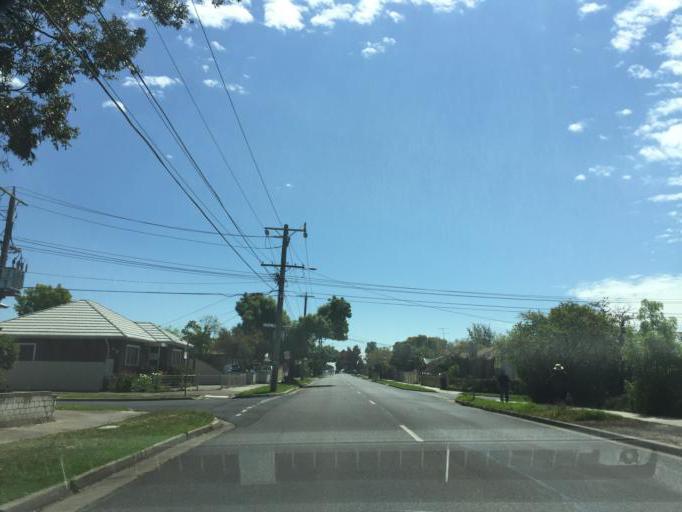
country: AU
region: Victoria
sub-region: Maribyrnong
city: Braybrook
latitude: -37.7816
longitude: 144.8468
